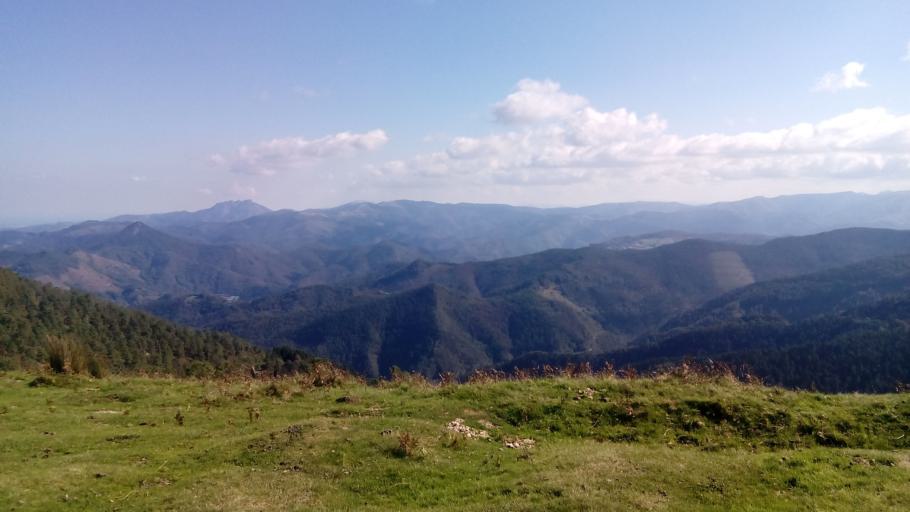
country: ES
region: Basque Country
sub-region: Provincia de Guipuzcoa
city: Urnieta
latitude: 43.1959
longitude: -1.9670
